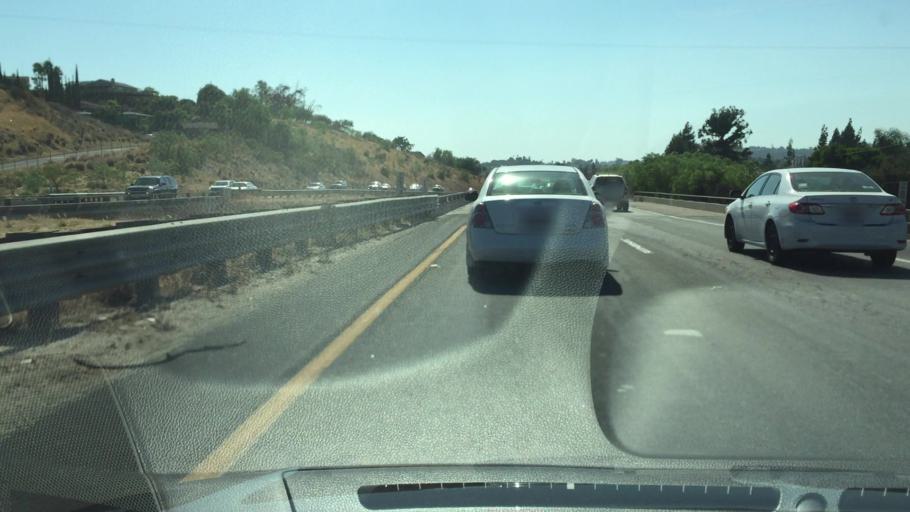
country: US
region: California
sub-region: San Diego County
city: Spring Valley
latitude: 32.7447
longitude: -116.9814
